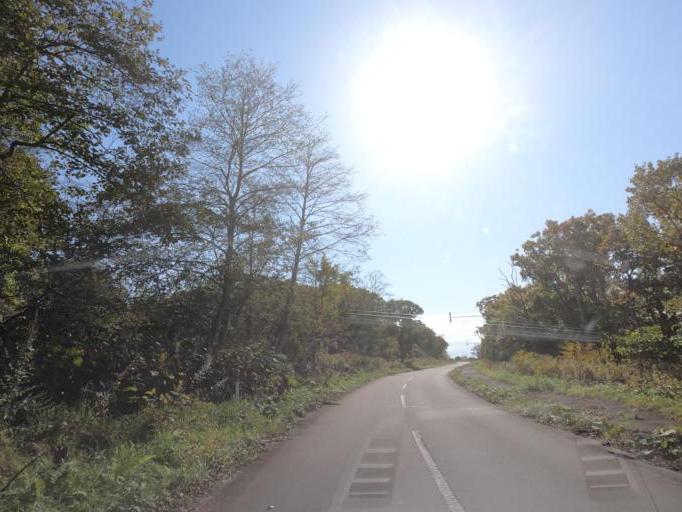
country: JP
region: Hokkaido
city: Obihiro
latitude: 42.6044
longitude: 143.5517
